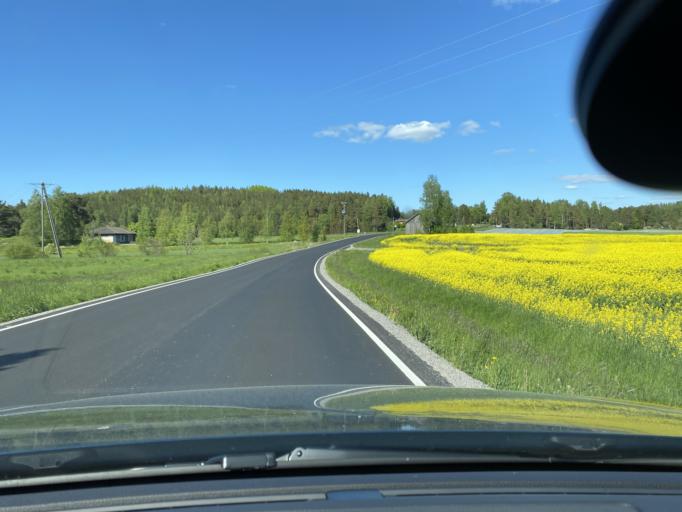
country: FI
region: Varsinais-Suomi
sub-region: Turku
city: Sauvo
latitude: 60.3322
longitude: 22.6802
